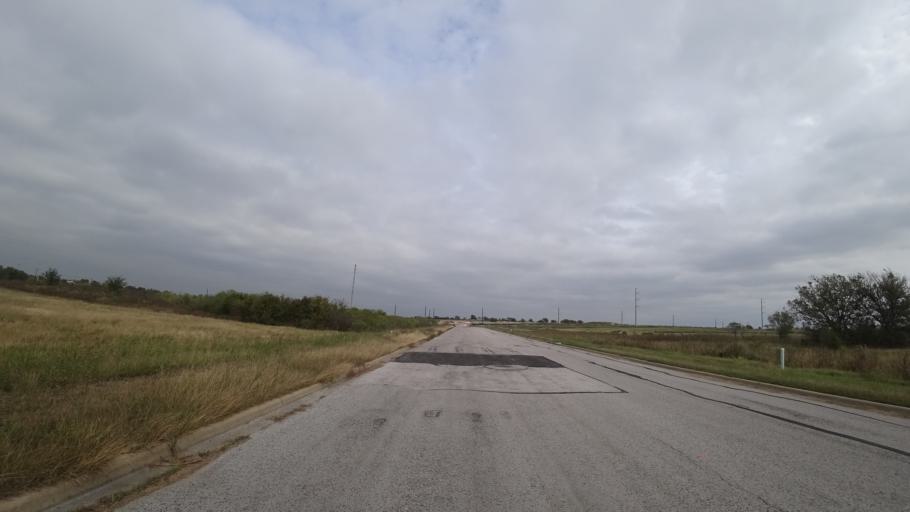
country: US
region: Texas
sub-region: Travis County
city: Manor
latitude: 30.3754
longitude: -97.6057
